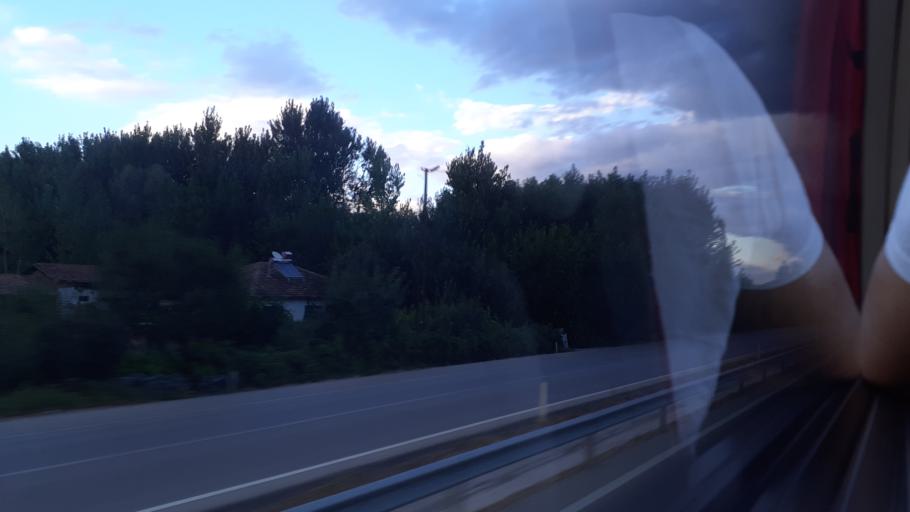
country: TR
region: Tokat
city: Dokmetepe
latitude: 40.3220
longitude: 36.2150
